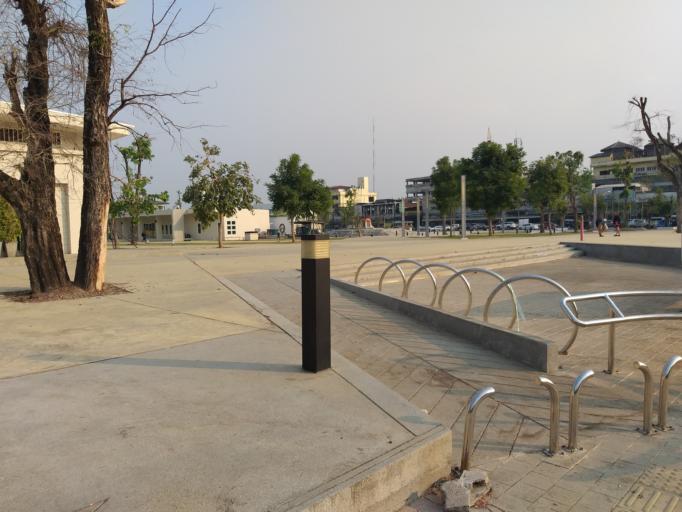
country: TH
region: Khon Kaen
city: Khon Kaen
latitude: 16.4398
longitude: 102.8350
